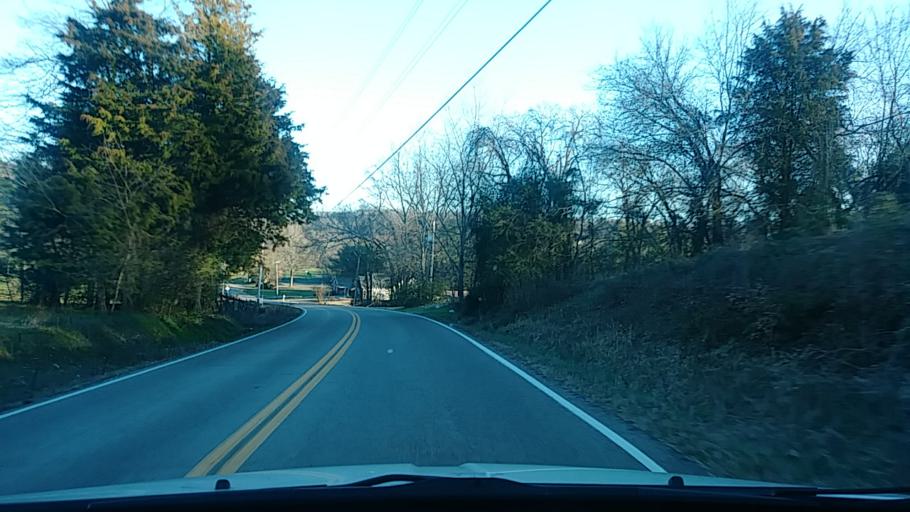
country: US
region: Tennessee
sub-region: Hamblen County
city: Morristown
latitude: 36.1975
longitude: -83.3985
